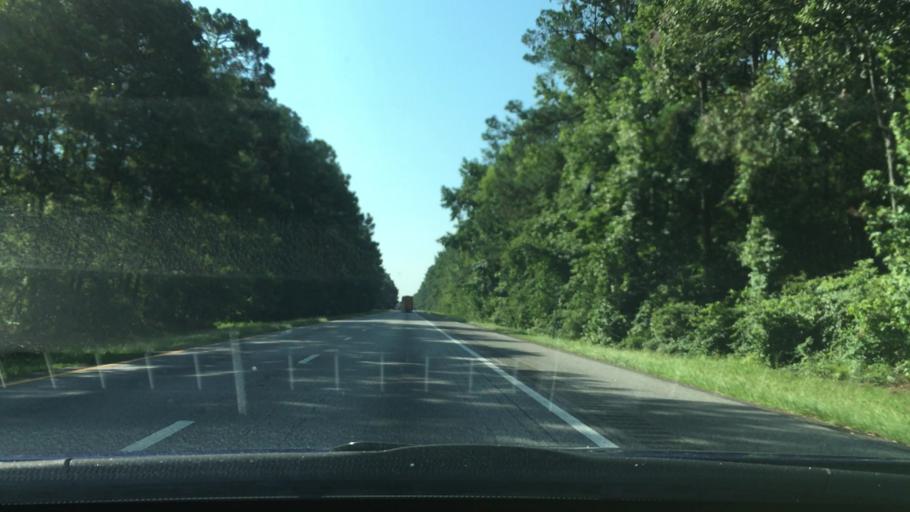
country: US
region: South Carolina
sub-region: Dorchester County
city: Ridgeville
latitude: 33.1645
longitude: -80.3586
